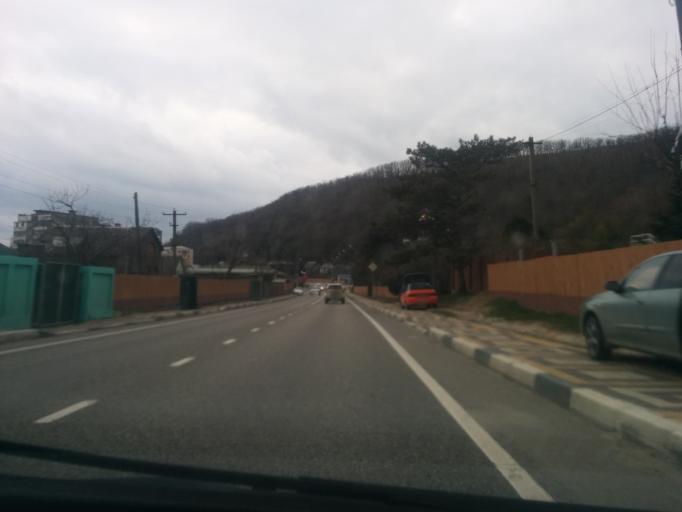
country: RU
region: Krasnodarskiy
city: Ol'ginka
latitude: 44.2053
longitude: 38.8890
